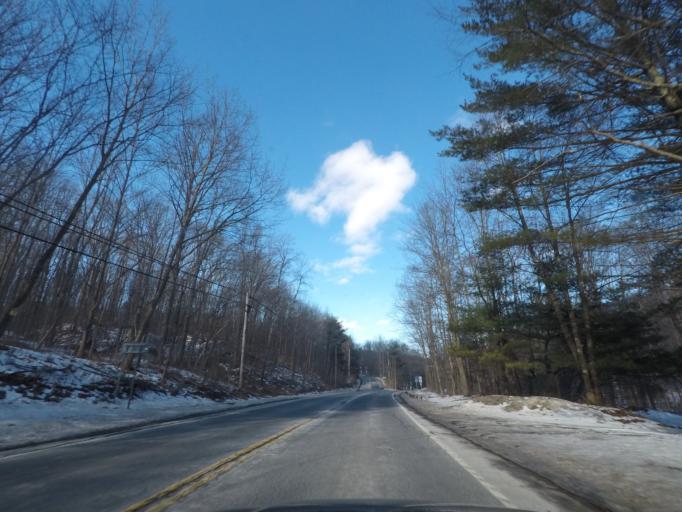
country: US
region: Massachusetts
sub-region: Berkshire County
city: West Stockbridge
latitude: 42.3151
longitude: -73.4725
